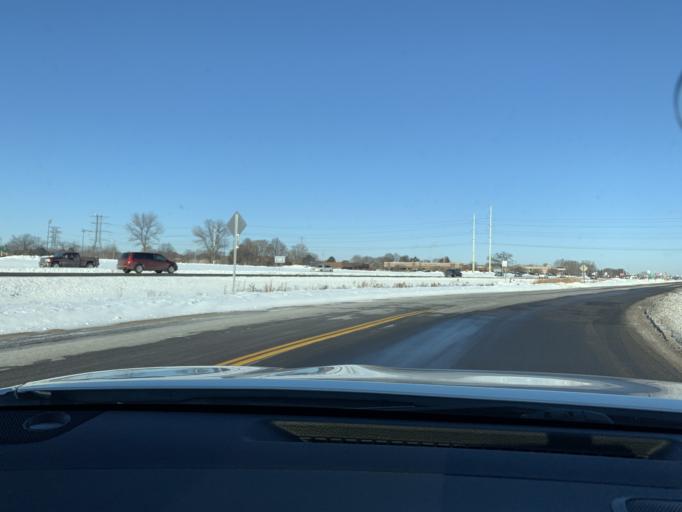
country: US
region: Minnesota
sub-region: Anoka County
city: Fridley
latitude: 45.0947
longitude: -93.2629
